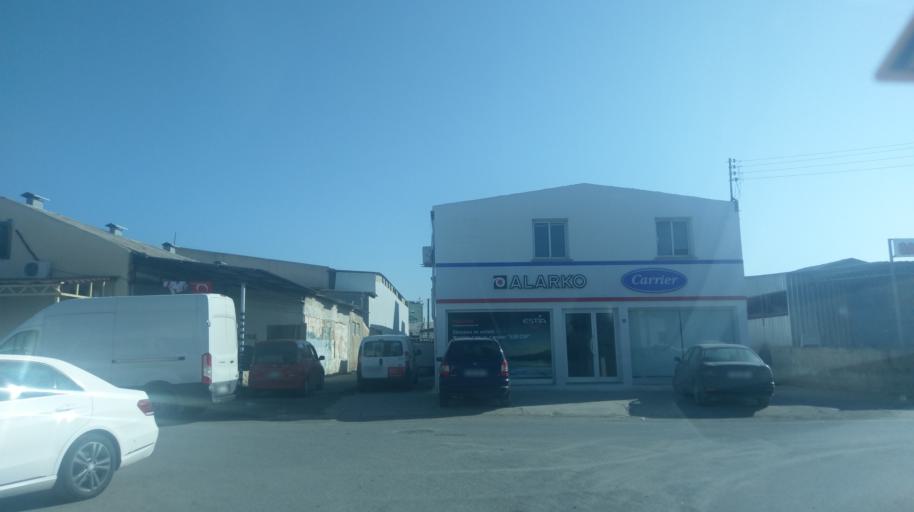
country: CY
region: Lefkosia
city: Nicosia
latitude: 35.2140
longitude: 33.3450
